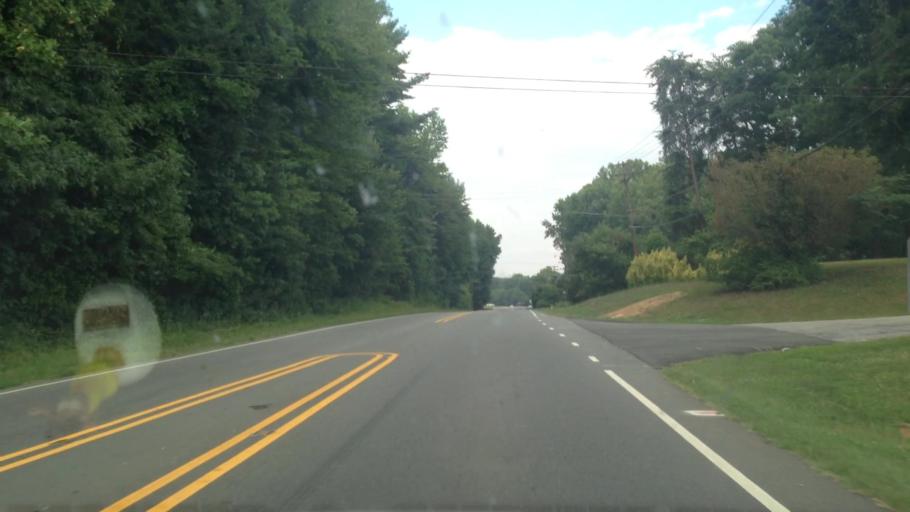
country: US
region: North Carolina
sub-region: Forsyth County
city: Kernersville
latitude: 36.1327
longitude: -80.0910
